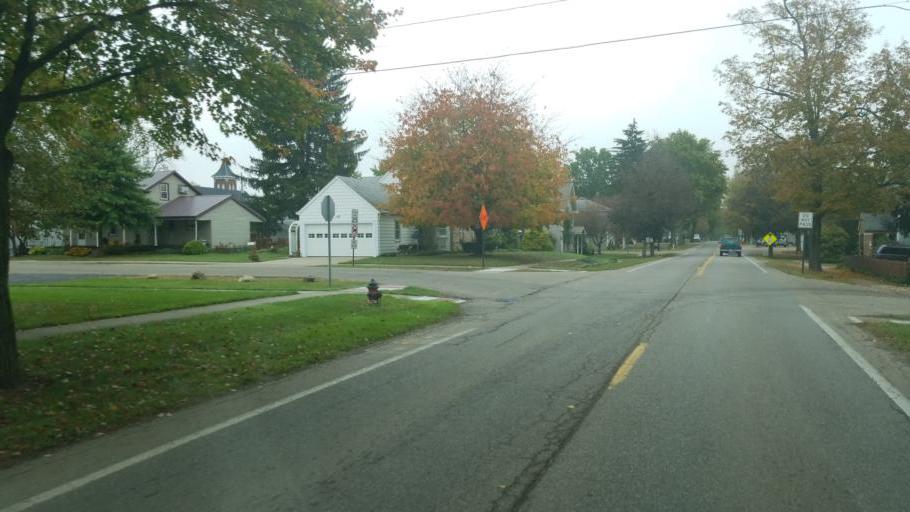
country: US
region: Ohio
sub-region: Tuscarawas County
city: Strasburg
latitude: 40.6486
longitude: -81.4529
